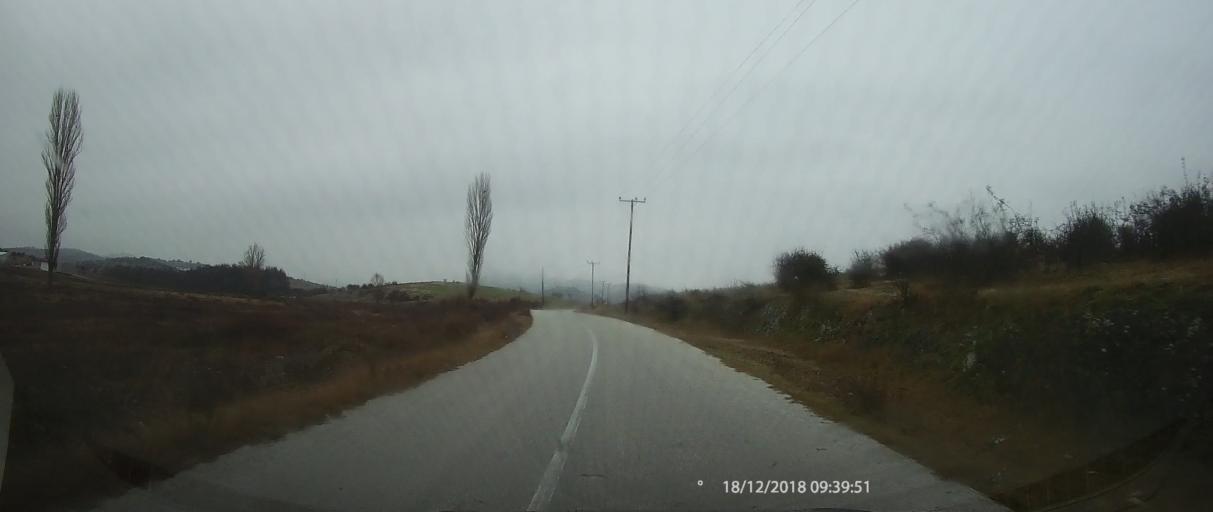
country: GR
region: Thessaly
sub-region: Nomos Larisis
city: Elassona
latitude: 40.0021
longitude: 22.2206
